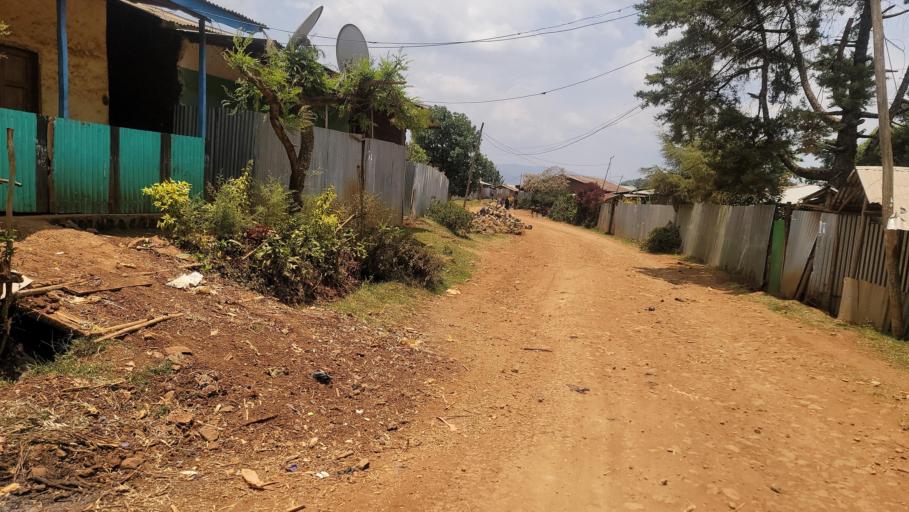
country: ET
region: Oromiya
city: Agaro
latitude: 7.7940
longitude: 36.4775
